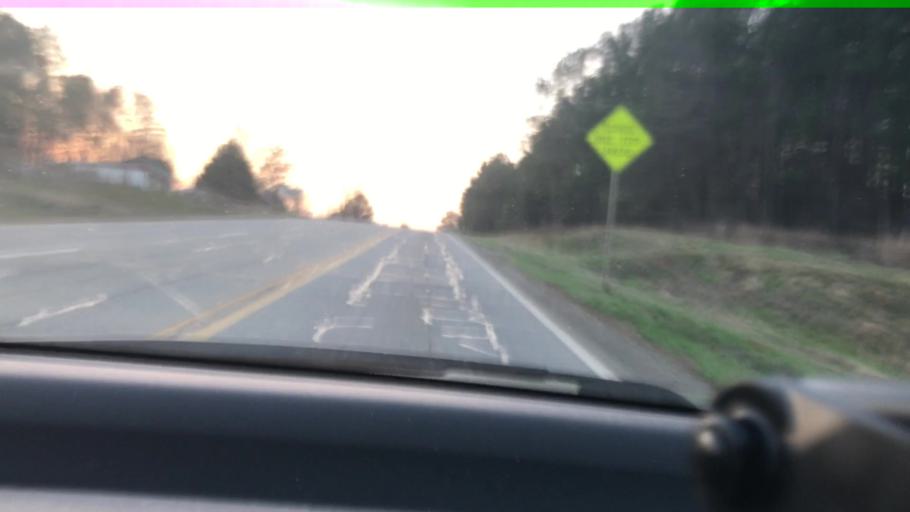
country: US
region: Georgia
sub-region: Oglethorpe County
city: Lexington
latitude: 33.8869
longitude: -83.1765
